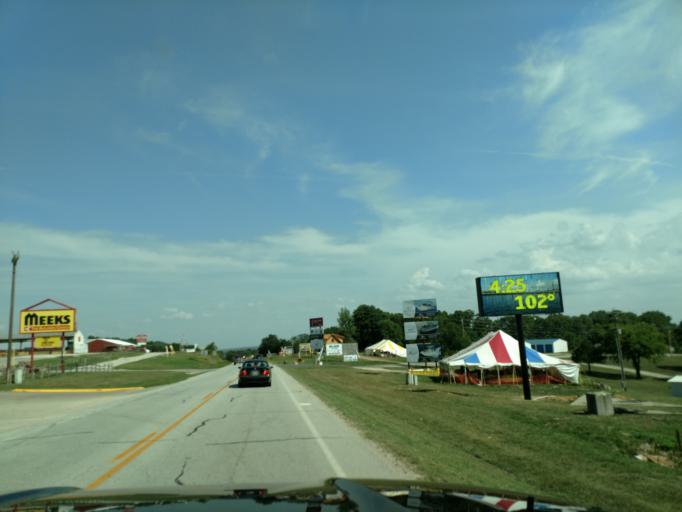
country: US
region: Missouri
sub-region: Barry County
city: Shell Knob
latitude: 36.6245
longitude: -93.6209
